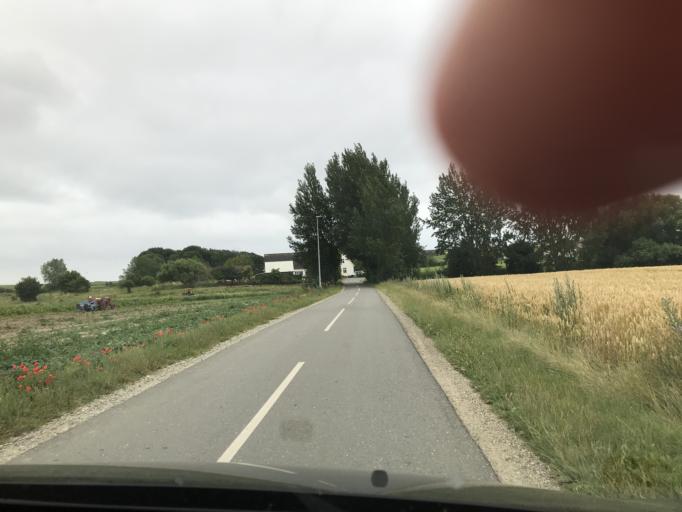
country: DK
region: South Denmark
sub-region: AEro Kommune
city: Marstal
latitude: 54.8487
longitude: 10.4769
